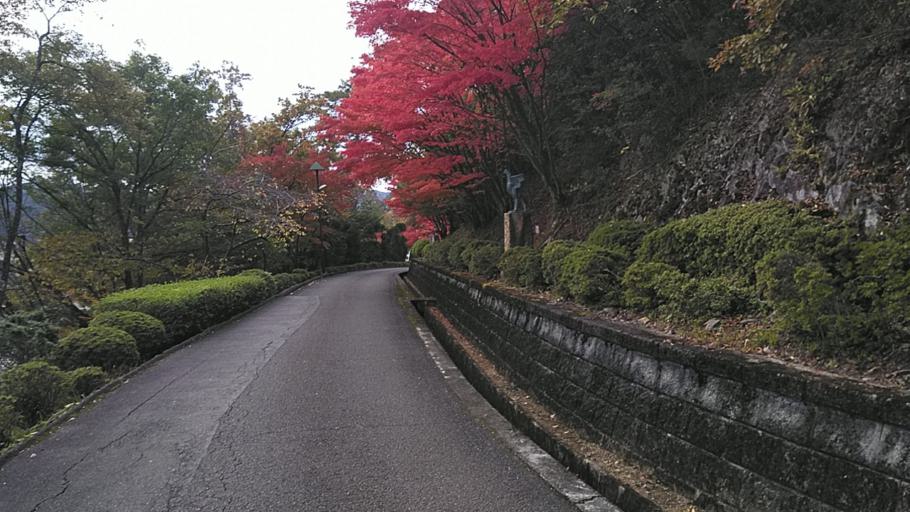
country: JP
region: Kyoto
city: Kameoka
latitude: 35.1991
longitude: 135.6340
